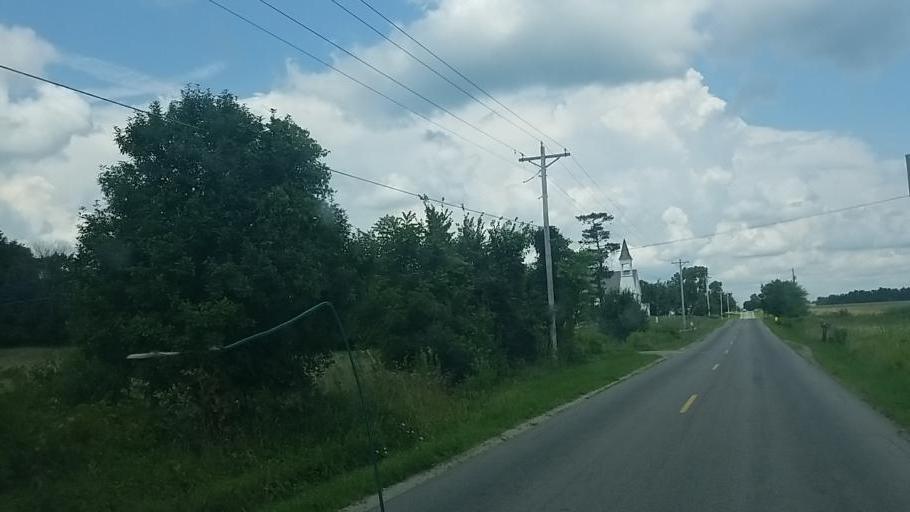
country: US
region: Ohio
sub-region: Medina County
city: Lodi
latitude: 41.0480
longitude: -82.0770
